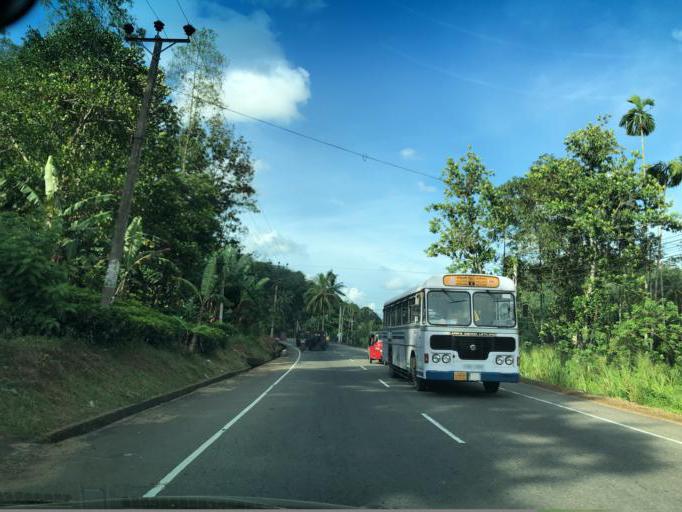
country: LK
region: Western
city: Horawala Junction
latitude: 6.5197
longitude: 80.0811
